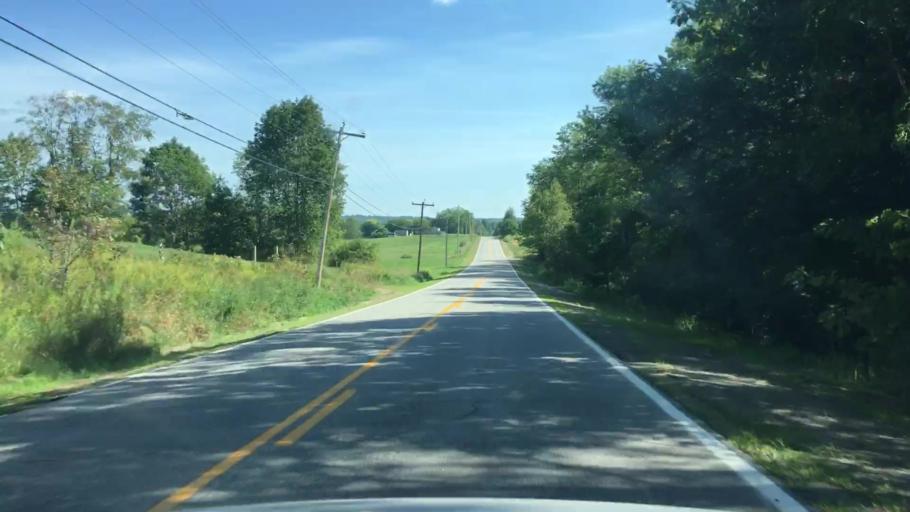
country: US
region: Maine
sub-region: Androscoggin County
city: Greene
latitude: 44.2179
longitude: -70.0902
